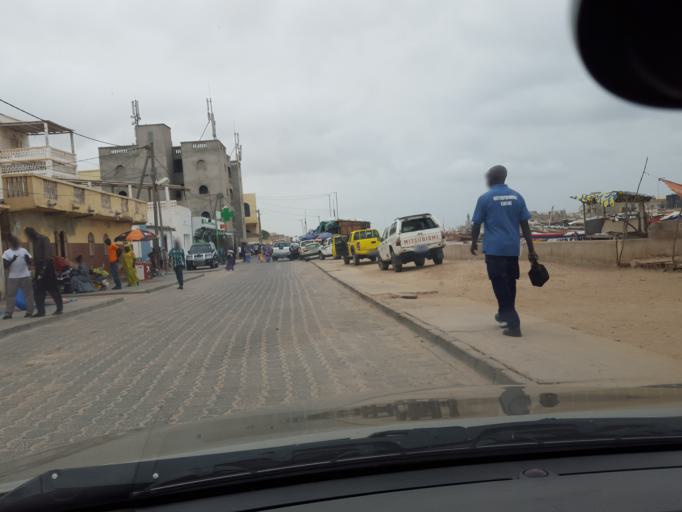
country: SN
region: Saint-Louis
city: Saint-Louis
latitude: 16.0246
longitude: -16.5062
